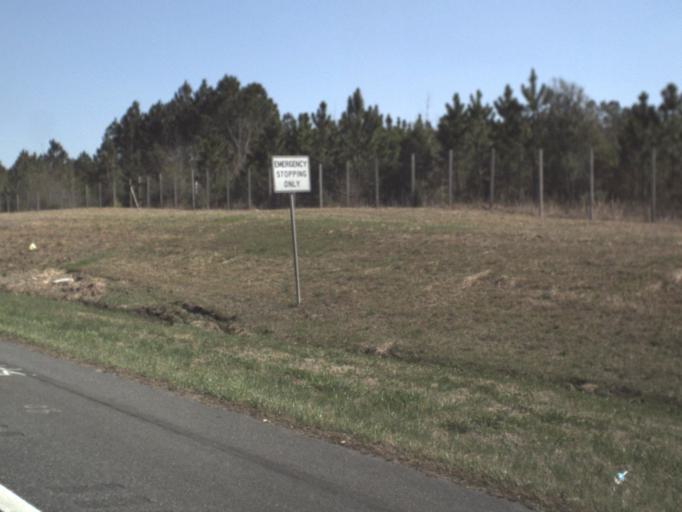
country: US
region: Florida
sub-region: Jackson County
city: Marianna
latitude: 30.7549
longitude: -85.3667
